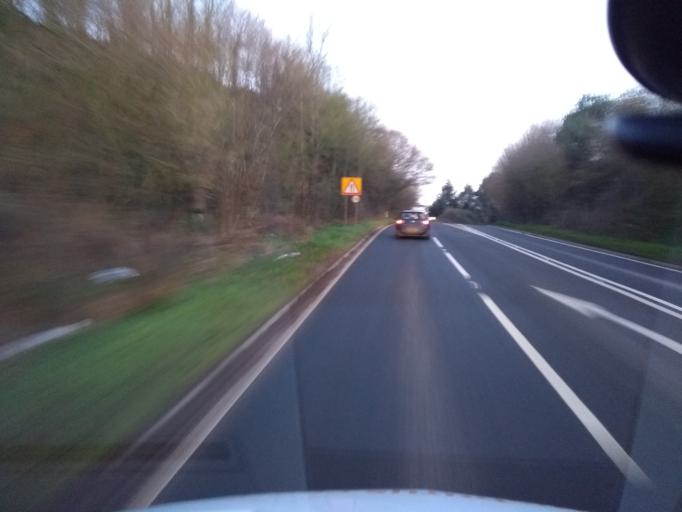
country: GB
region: England
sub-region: Somerset
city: Creech Saint Michael
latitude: 51.0558
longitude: -3.0366
